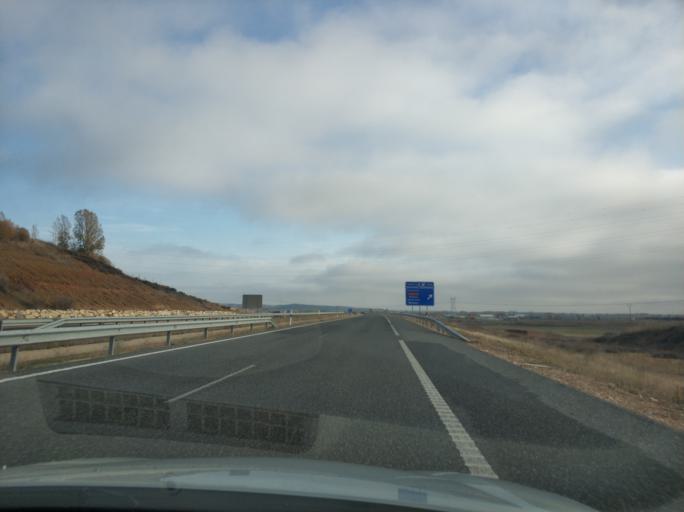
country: ES
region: Castille and Leon
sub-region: Provincia de Leon
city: Valdefresno
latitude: 42.5602
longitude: -5.4748
